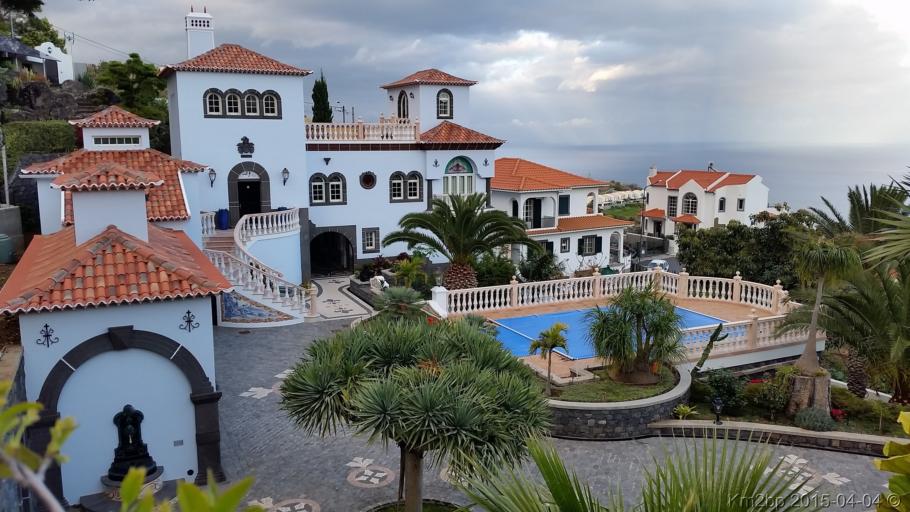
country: PT
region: Madeira
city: Canico
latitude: 32.6499
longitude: -16.8371
